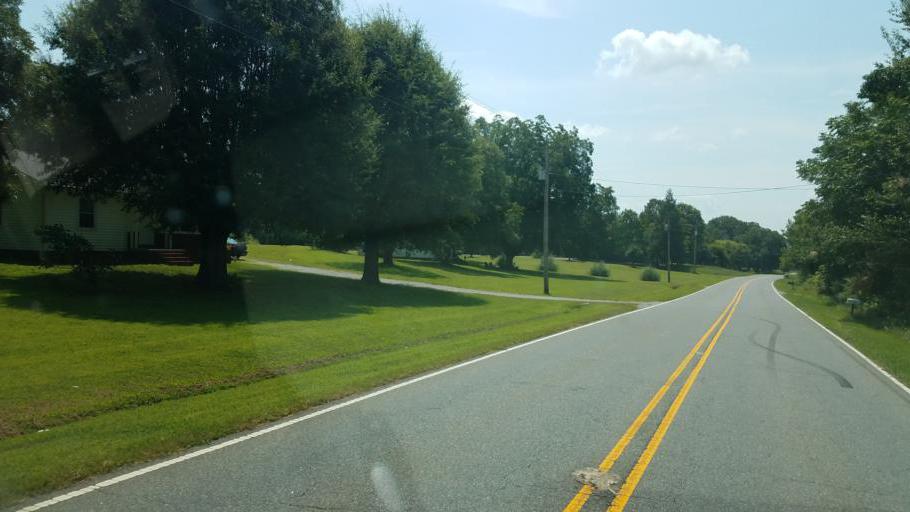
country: US
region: North Carolina
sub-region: Gaston County
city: Cherryville
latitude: 35.4016
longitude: -81.3970
